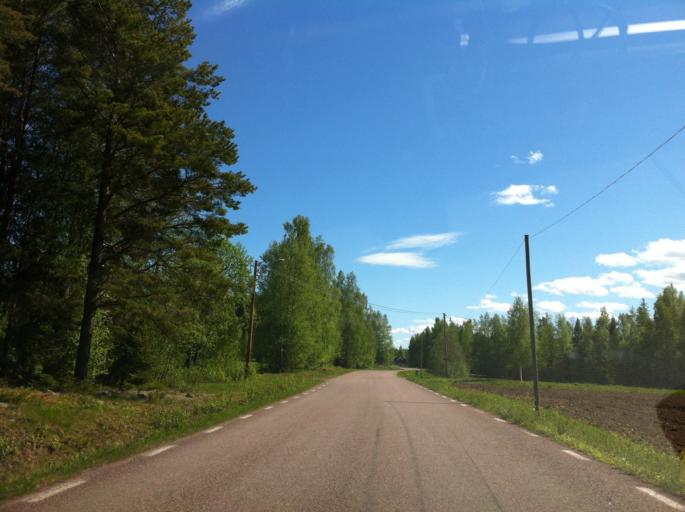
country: SE
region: Dalarna
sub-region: Mora Kommun
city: Mora
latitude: 60.9807
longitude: 14.6292
